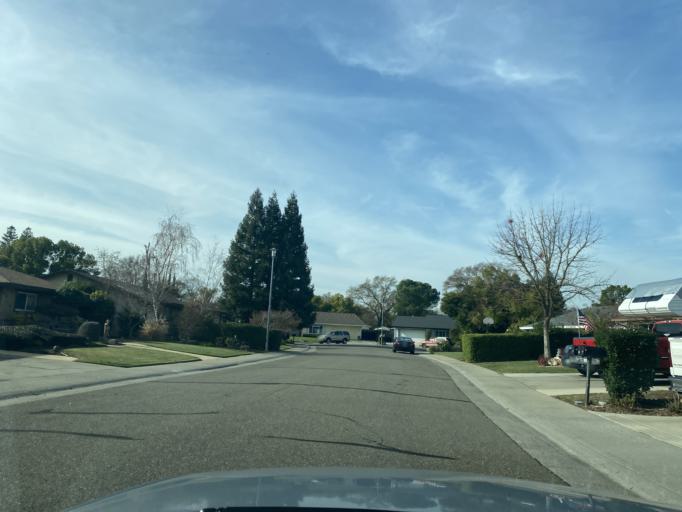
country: US
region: California
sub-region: Sacramento County
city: Elk Grove
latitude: 38.4039
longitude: -121.3799
